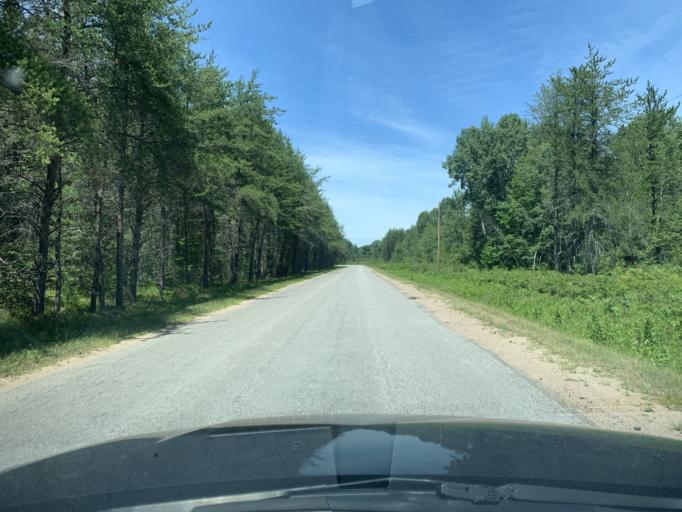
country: CA
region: Ontario
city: Petawawa
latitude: 45.6596
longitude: -77.6057
